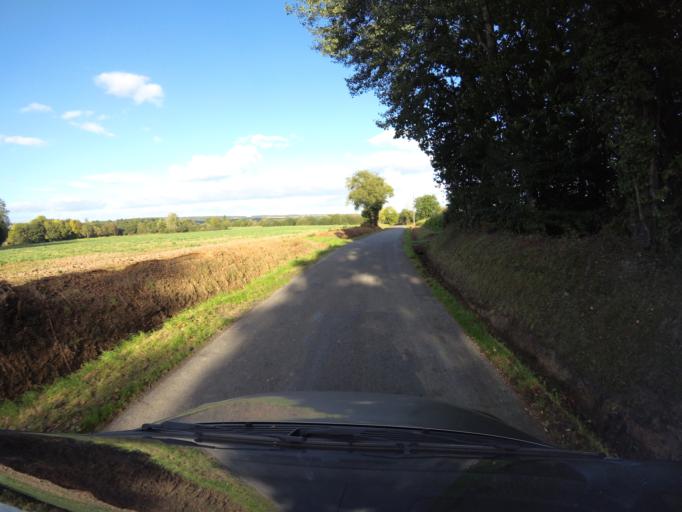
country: FR
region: Brittany
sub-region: Departement du Morbihan
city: Peillac
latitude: 47.7153
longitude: -2.1835
